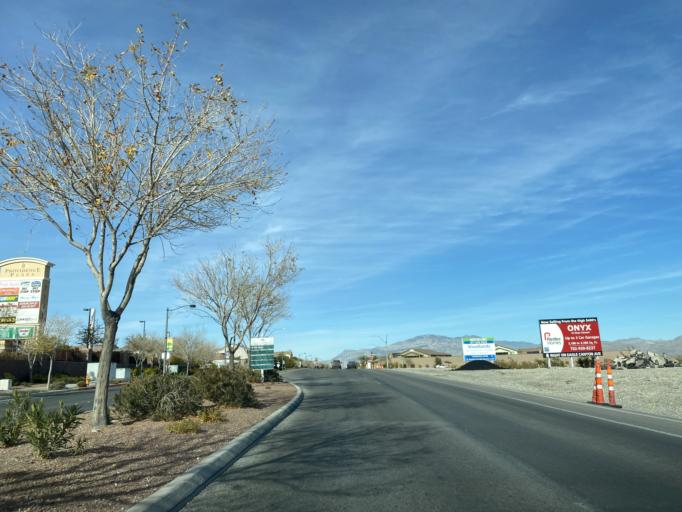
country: US
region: Nevada
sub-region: Clark County
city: Summerlin South
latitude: 36.2906
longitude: -115.3148
